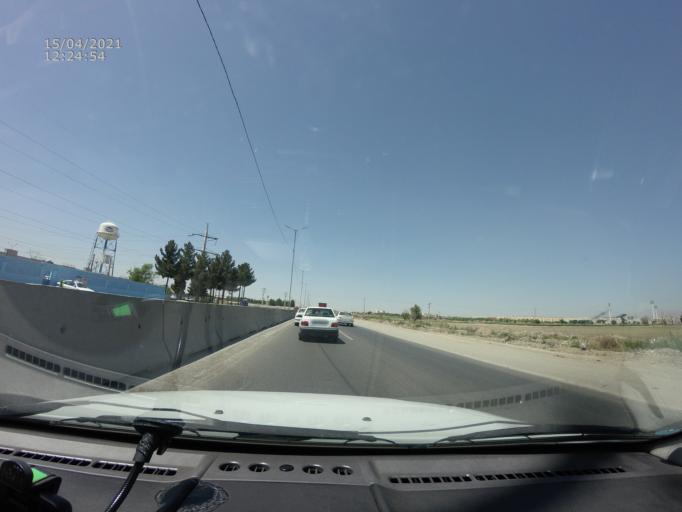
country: IR
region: Tehran
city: Eslamshahr
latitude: 35.5120
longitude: 51.2513
